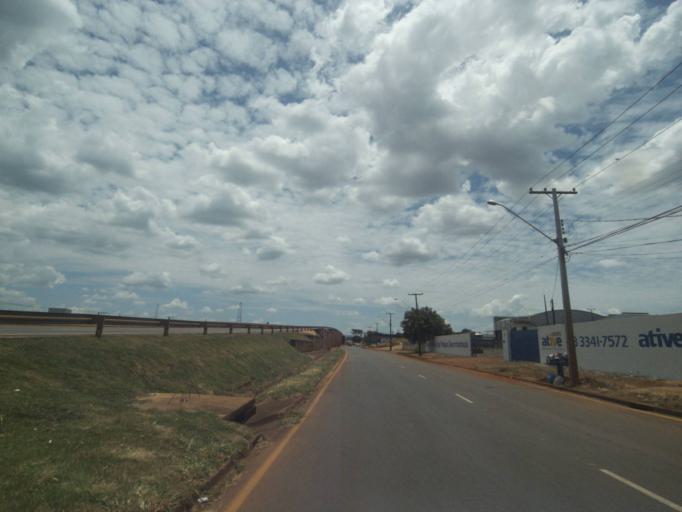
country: BR
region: Parana
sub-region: Londrina
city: Londrina
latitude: -23.3611
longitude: -51.1492
